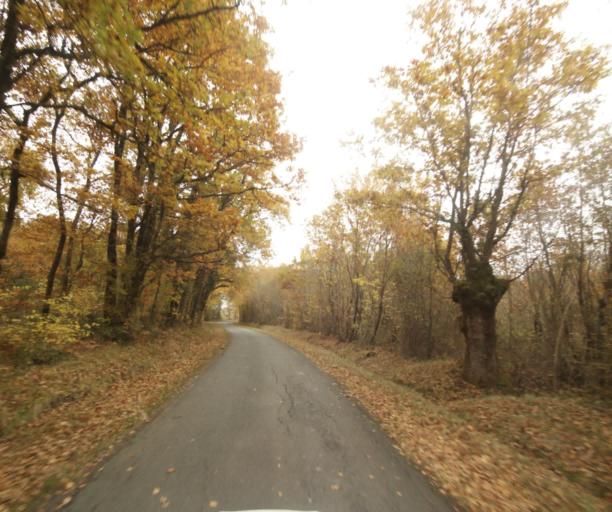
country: FR
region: Poitou-Charentes
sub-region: Departement de la Charente-Maritime
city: Chermignac
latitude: 45.7088
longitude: -0.6704
